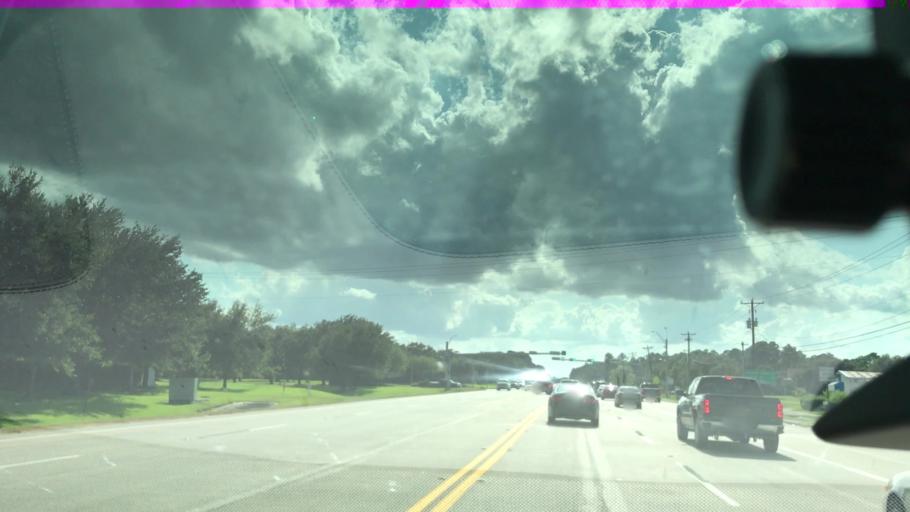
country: US
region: Texas
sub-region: Galveston County
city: League City
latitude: 29.4963
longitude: -95.1380
